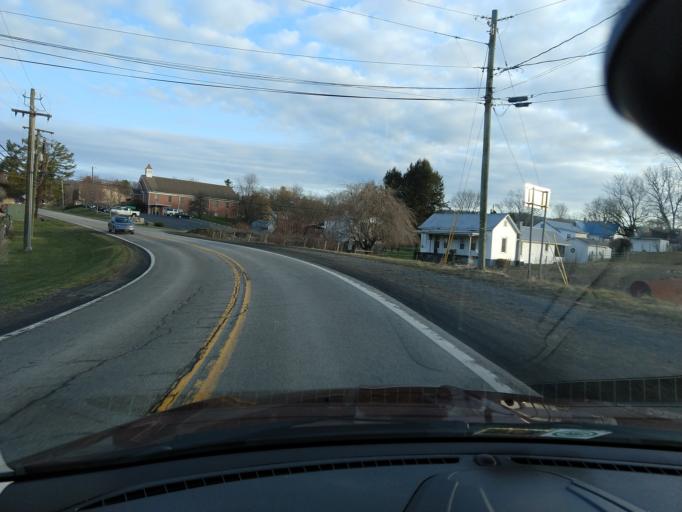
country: US
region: West Virginia
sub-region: Greenbrier County
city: White Sulphur Springs
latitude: 37.9934
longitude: -80.3617
